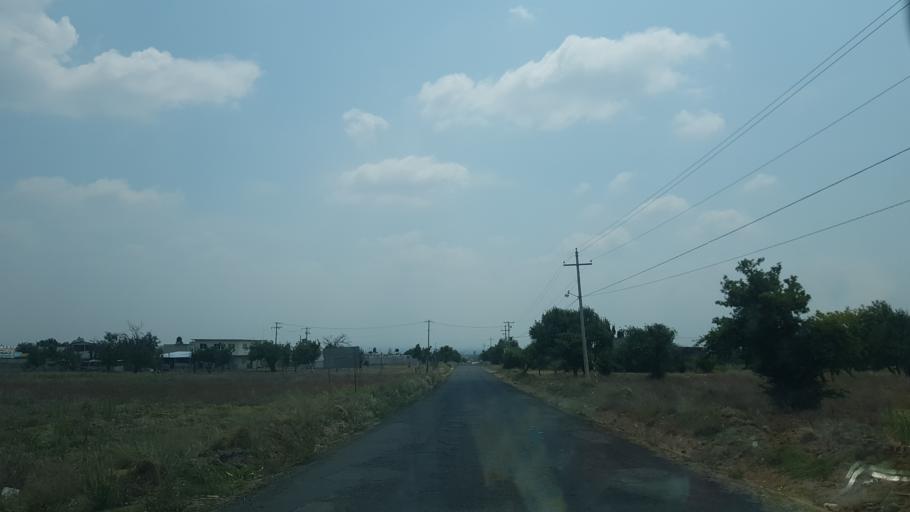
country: MX
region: Puebla
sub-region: Huejotzingo
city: San Juan Pancoac
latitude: 19.1373
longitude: -98.4213
